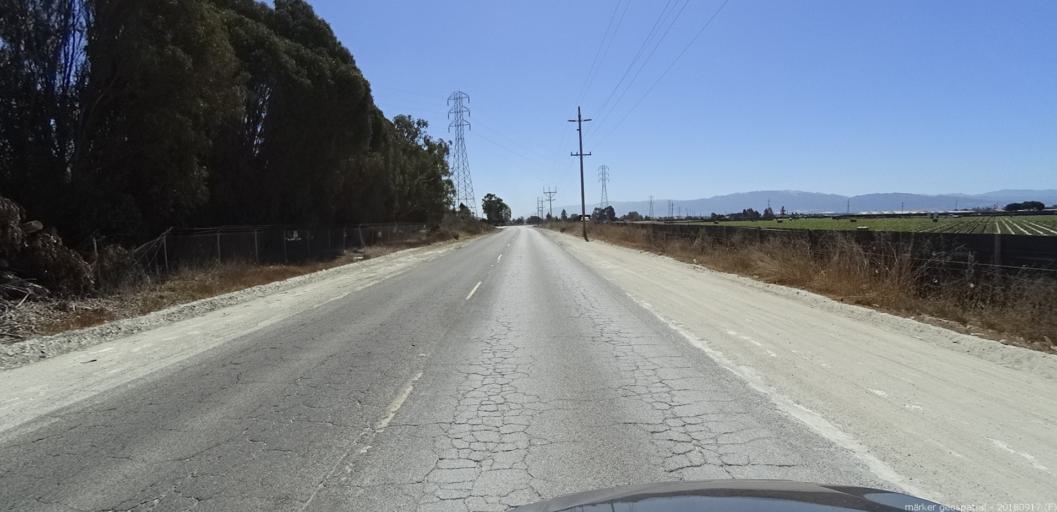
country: US
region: California
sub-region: Monterey County
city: Prunedale
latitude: 36.7451
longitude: -121.6043
